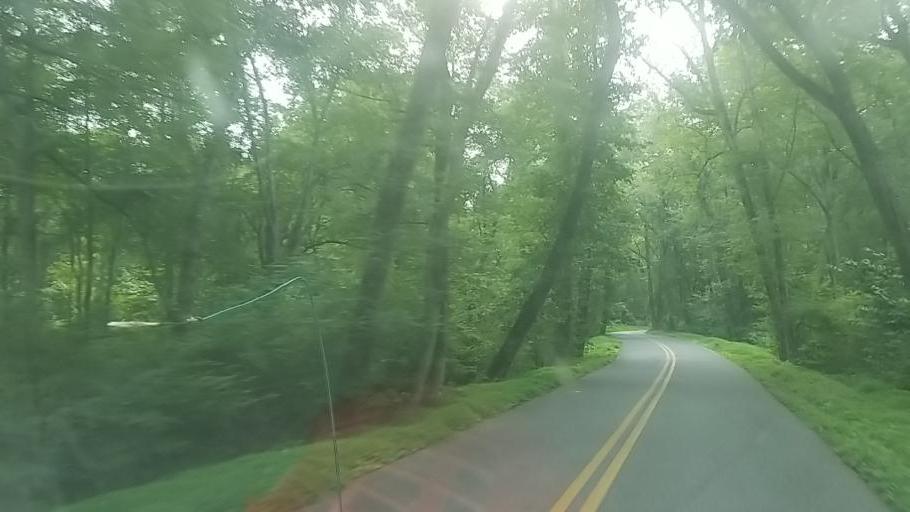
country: US
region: Maryland
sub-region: Wicomico County
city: Pittsville
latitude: 38.4407
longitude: -75.3332
